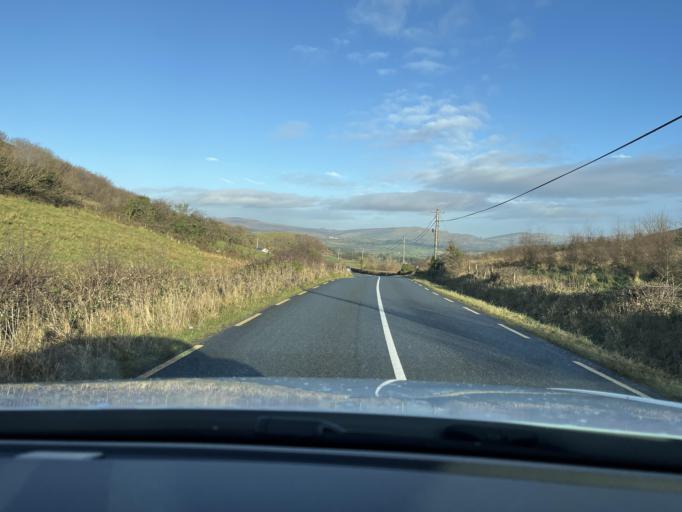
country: IE
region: Connaught
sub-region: County Leitrim
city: Manorhamilton
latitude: 54.2855
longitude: -8.2620
